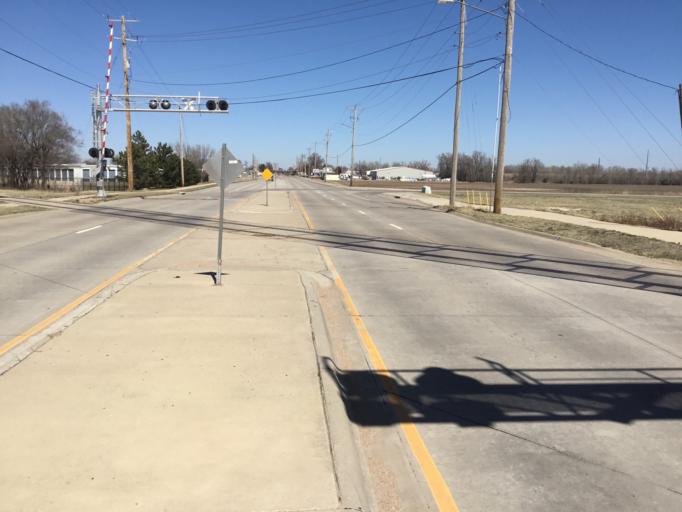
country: US
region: Kansas
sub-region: Sedgwick County
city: Maize
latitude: 37.7747
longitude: -97.4631
